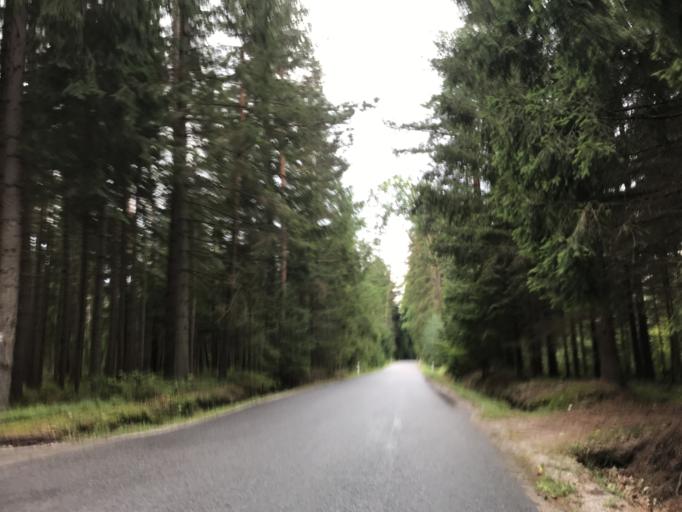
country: CZ
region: Jihocesky
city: Suchdol nad Luznici
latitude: 48.9380
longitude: 14.8528
